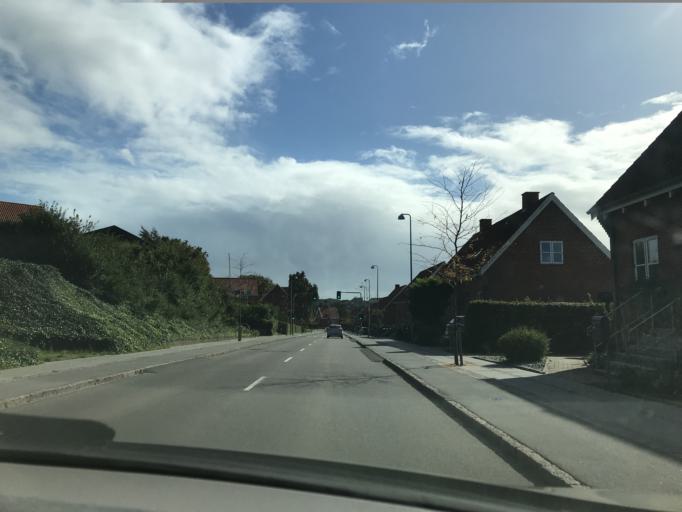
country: DK
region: Central Jutland
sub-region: Skanderborg Kommune
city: Skanderborg
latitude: 56.0361
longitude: 9.9204
